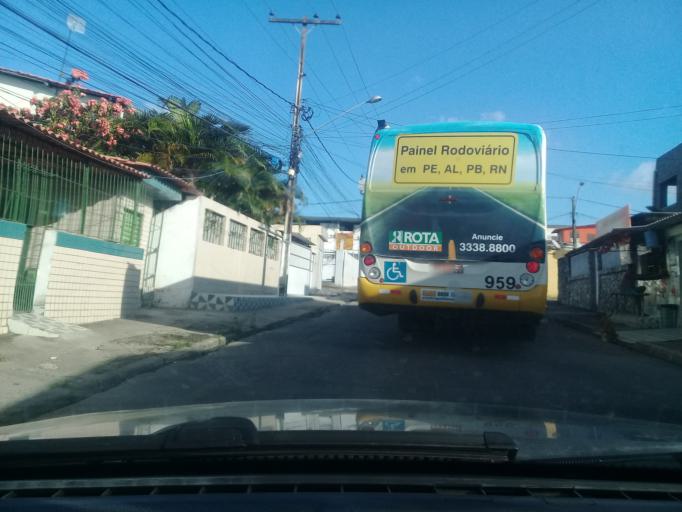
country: BR
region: Pernambuco
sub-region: Jaboatao Dos Guararapes
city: Jaboatao dos Guararapes
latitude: -8.1052
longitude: -34.9638
